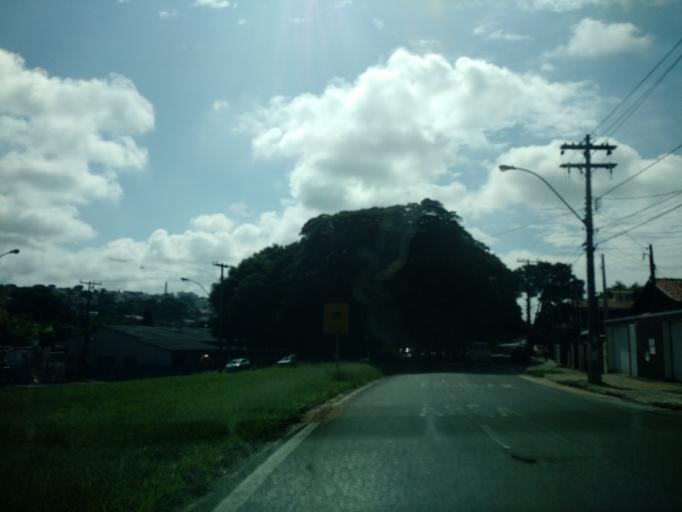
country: BR
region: Sao Paulo
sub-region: Campinas
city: Campinas
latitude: -22.8778
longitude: -47.0356
